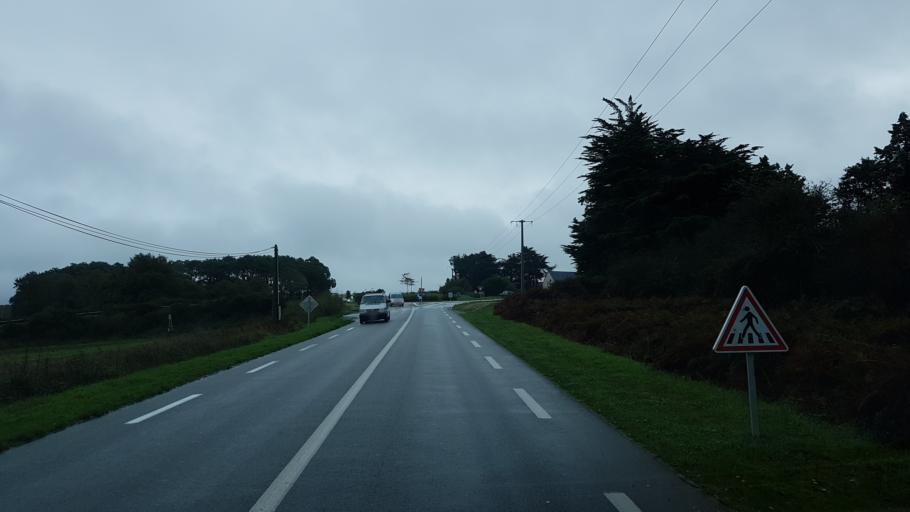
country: FR
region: Brittany
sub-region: Departement du Morbihan
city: Sarzeau
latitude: 47.5274
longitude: -2.7961
